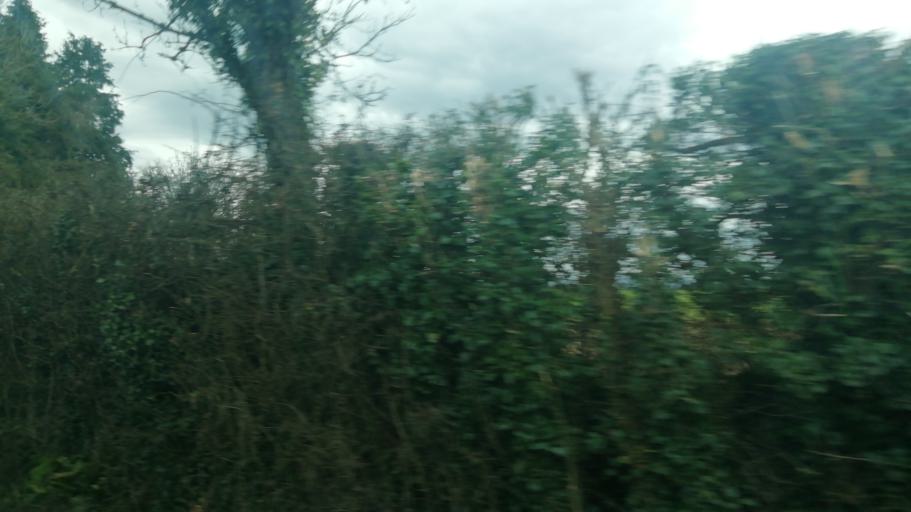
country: IE
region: Leinster
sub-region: Kildare
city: Prosperous
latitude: 53.3061
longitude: -6.7256
